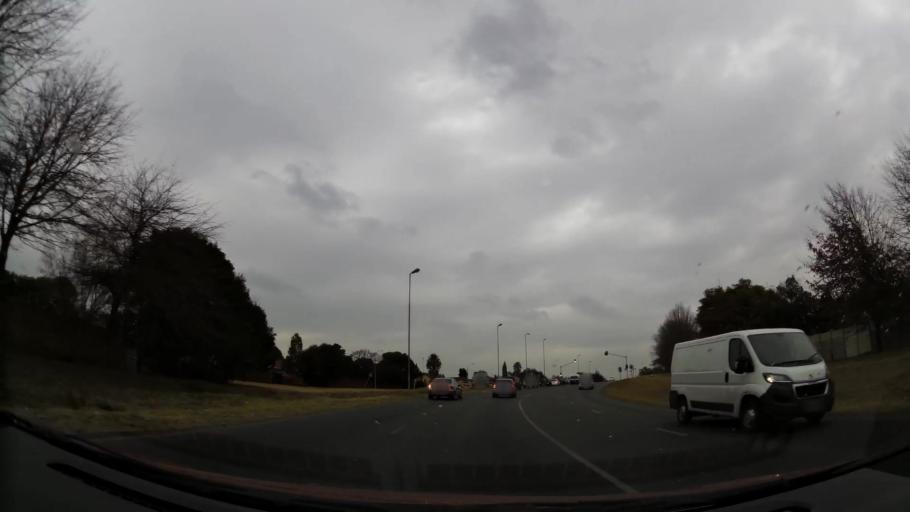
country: ZA
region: Gauteng
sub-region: City of Johannesburg Metropolitan Municipality
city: Roodepoort
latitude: -26.1444
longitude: 27.9018
